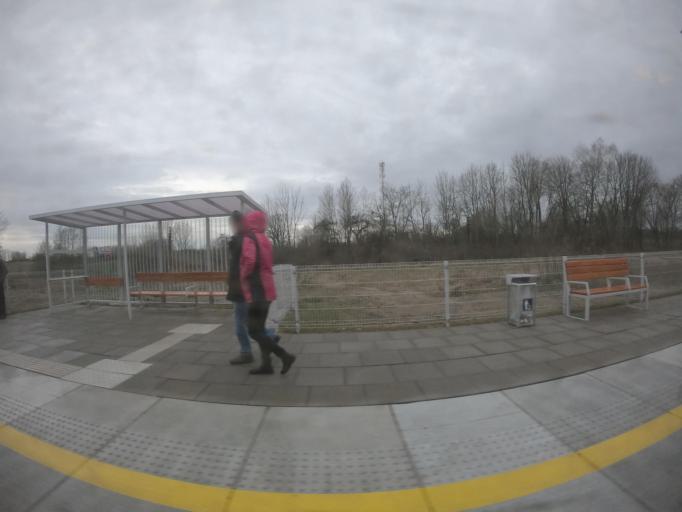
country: PL
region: West Pomeranian Voivodeship
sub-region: Powiat szczecinecki
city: Borne Sulinowo
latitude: 53.6353
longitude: 16.4920
